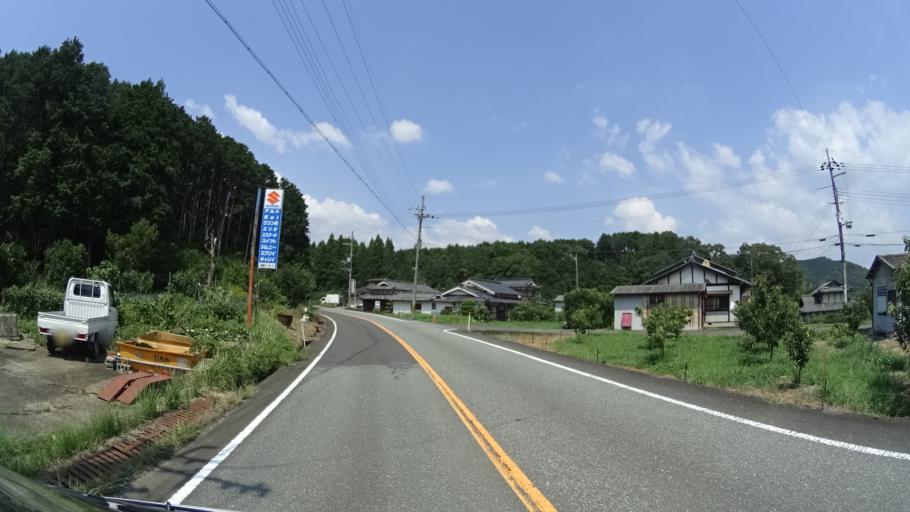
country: JP
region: Kyoto
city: Fukuchiyama
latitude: 35.2540
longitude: 135.1483
